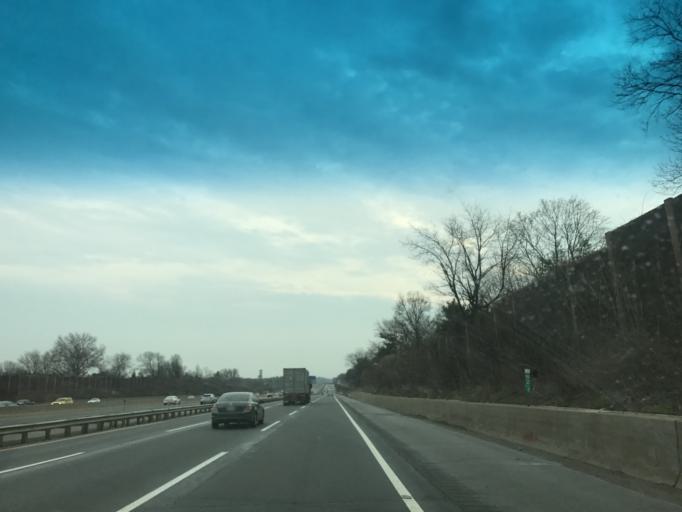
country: US
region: New Jersey
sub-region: Middlesex County
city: Milltown
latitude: 40.4620
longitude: -74.4162
